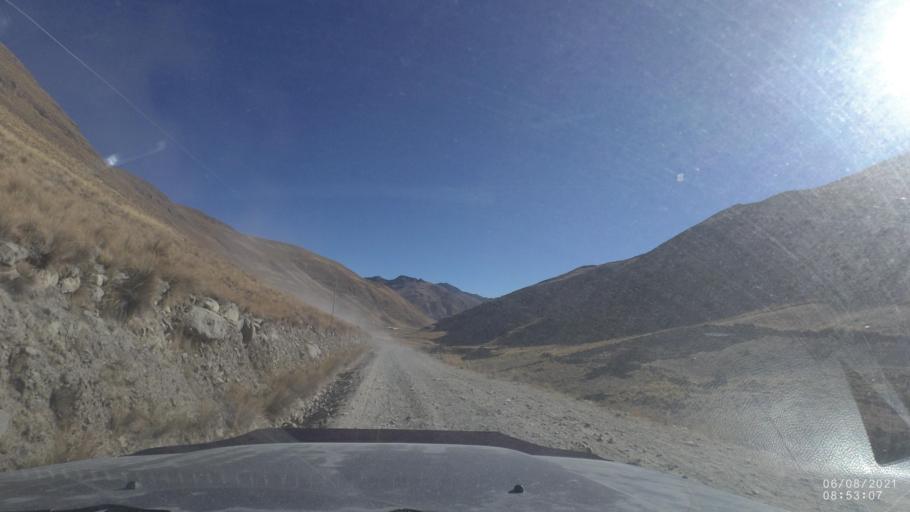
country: BO
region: Cochabamba
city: Sipe Sipe
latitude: -17.1319
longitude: -66.4397
